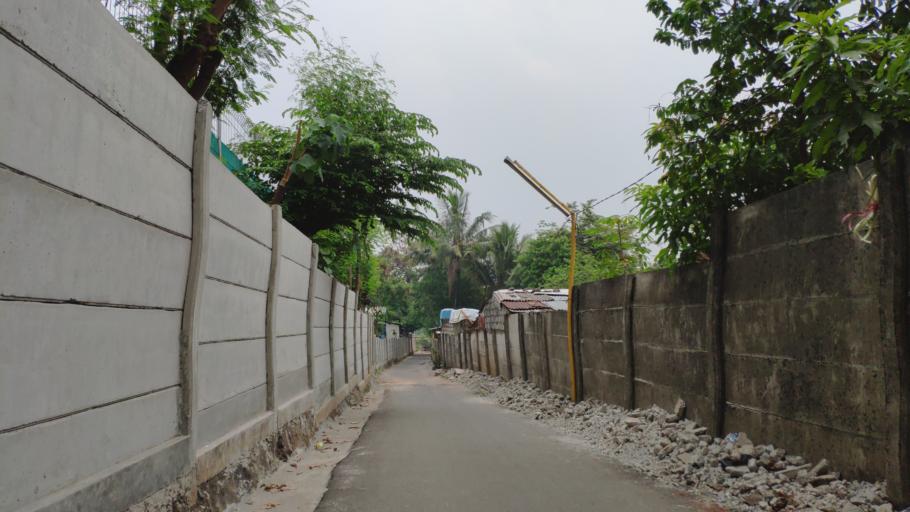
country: ID
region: Banten
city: South Tangerang
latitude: -6.2676
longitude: 106.7674
